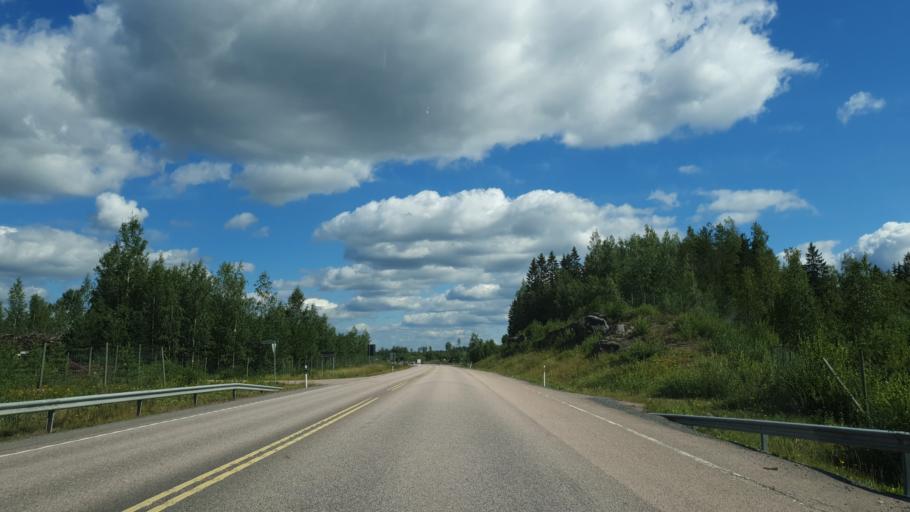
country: FI
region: Pirkanmaa
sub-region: Tampere
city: Kuhmalahti
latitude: 61.7076
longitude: 24.5750
